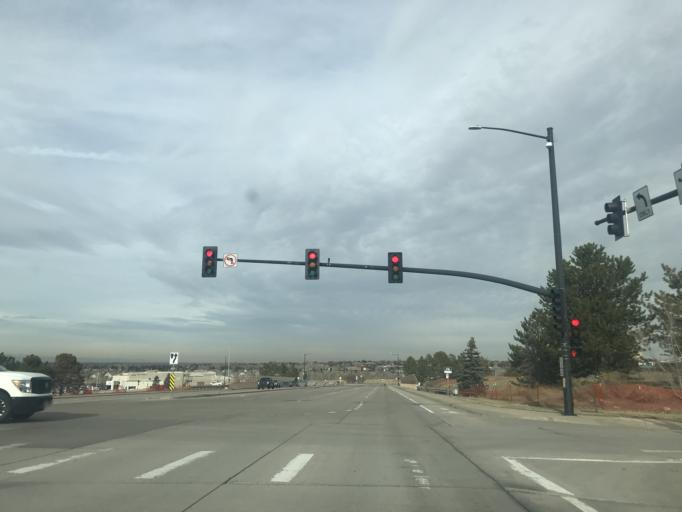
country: US
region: Colorado
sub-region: Douglas County
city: Highlands Ranch
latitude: 39.5586
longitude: -105.0080
